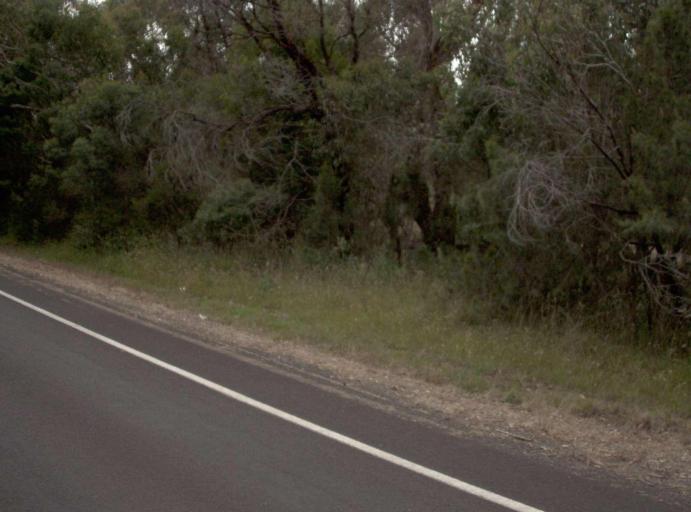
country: AU
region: Victoria
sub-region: Wellington
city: Sale
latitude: -38.4235
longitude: 146.9563
